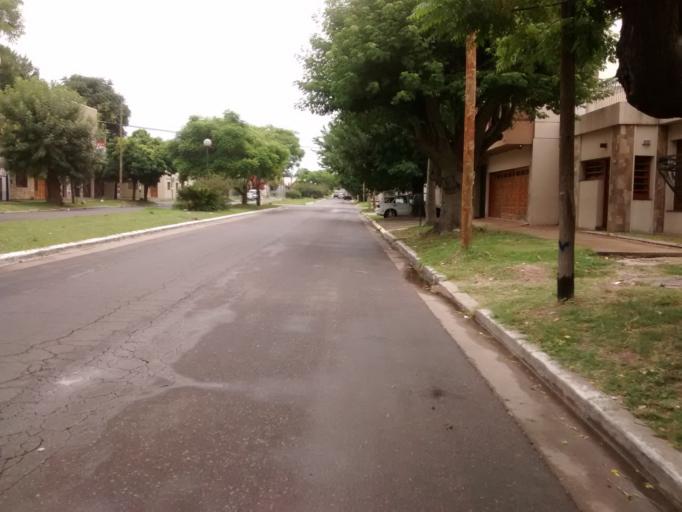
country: AR
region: Buenos Aires
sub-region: Partido de La Plata
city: La Plata
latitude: -34.8951
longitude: -57.9752
